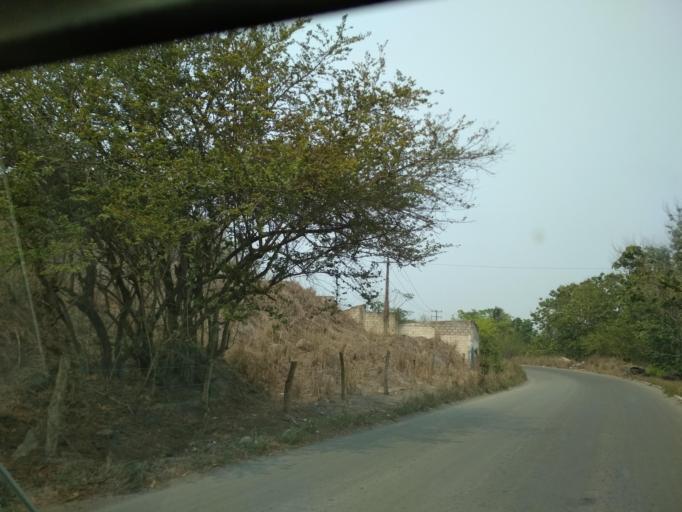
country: MX
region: Veracruz
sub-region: Veracruz
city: Delfino Victoria (Santa Fe)
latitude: 19.1838
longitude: -96.3199
